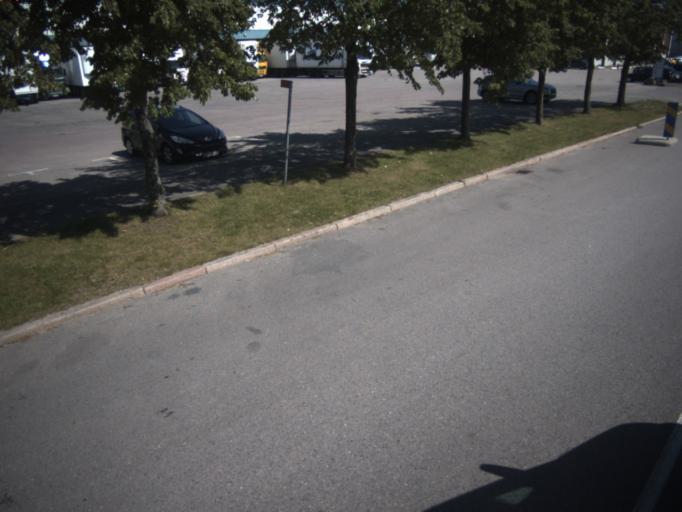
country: SE
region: Skane
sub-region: Helsingborg
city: Gantofta
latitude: 56.0088
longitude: 12.7675
